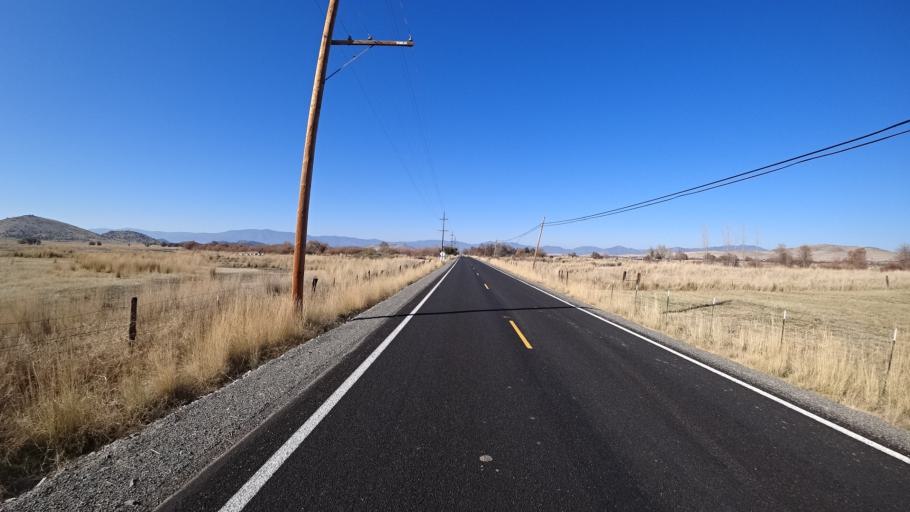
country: US
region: California
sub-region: Siskiyou County
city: Montague
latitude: 41.7114
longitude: -122.3815
